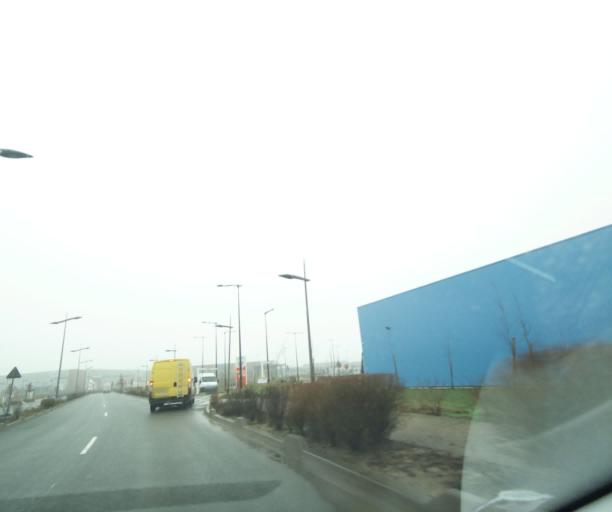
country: FR
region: Ile-de-France
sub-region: Departement de Seine-et-Marne
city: Saint-Mard
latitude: 49.0367
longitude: 2.6827
